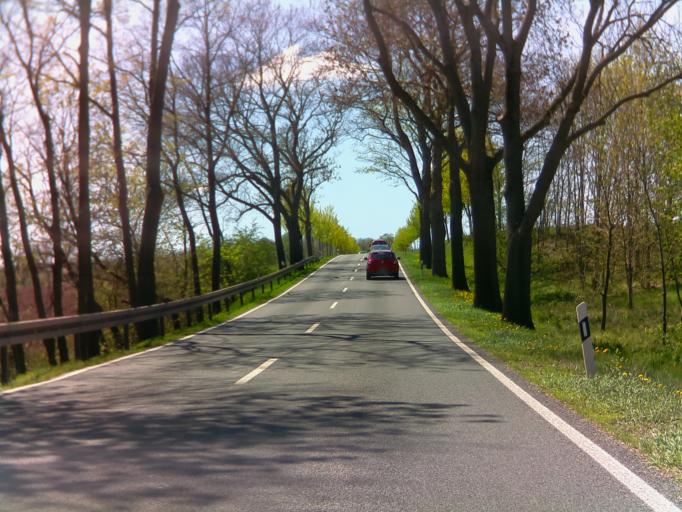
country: DE
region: Thuringia
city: Behringen
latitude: 50.7457
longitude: 11.0321
